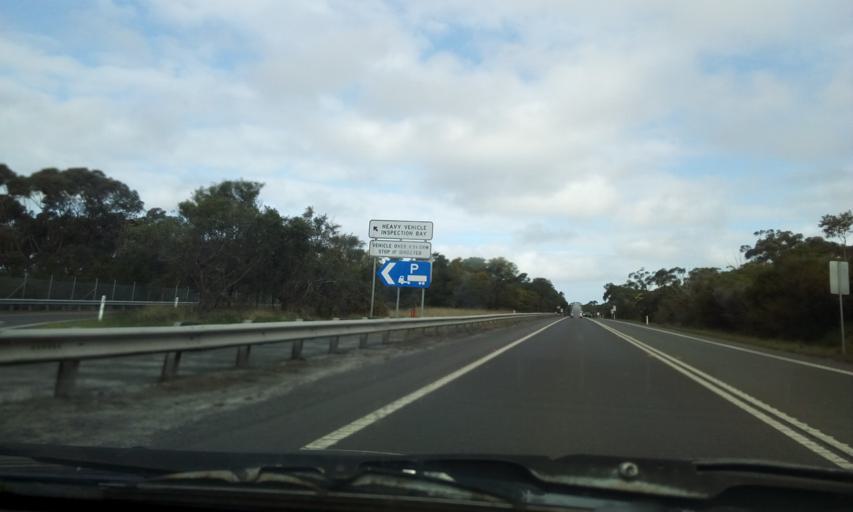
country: AU
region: New South Wales
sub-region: Wollongong
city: Bulli
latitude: -34.2577
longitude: 150.8732
